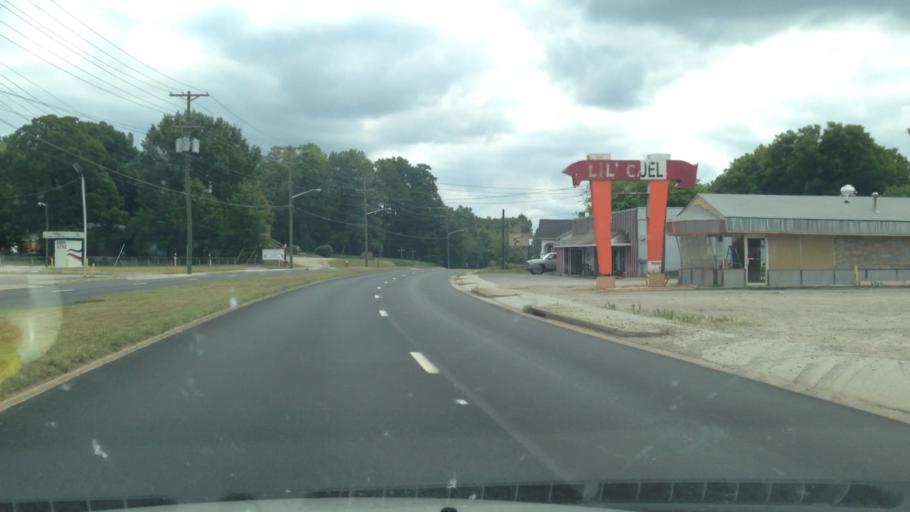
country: US
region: Virginia
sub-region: City of Danville
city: Danville
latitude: 36.5632
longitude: -79.4503
